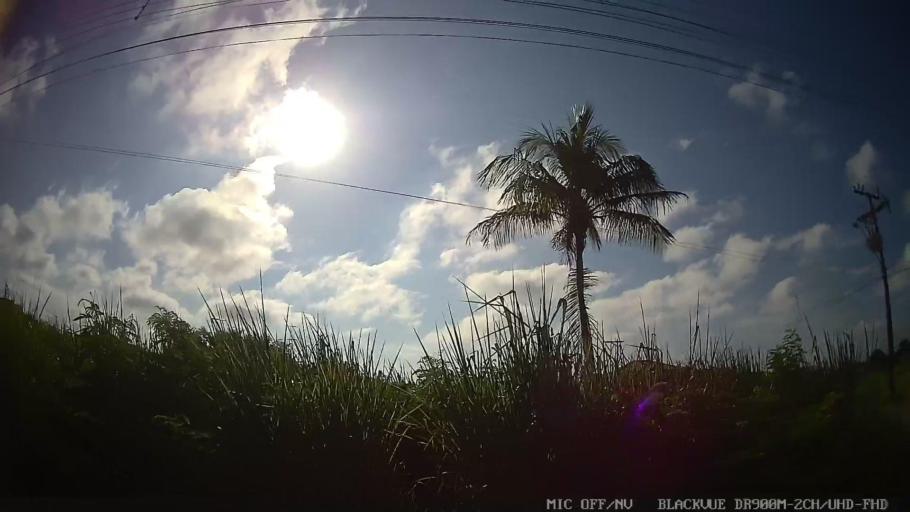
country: BR
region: Sao Paulo
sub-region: Peruibe
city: Peruibe
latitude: -24.2871
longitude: -46.9587
